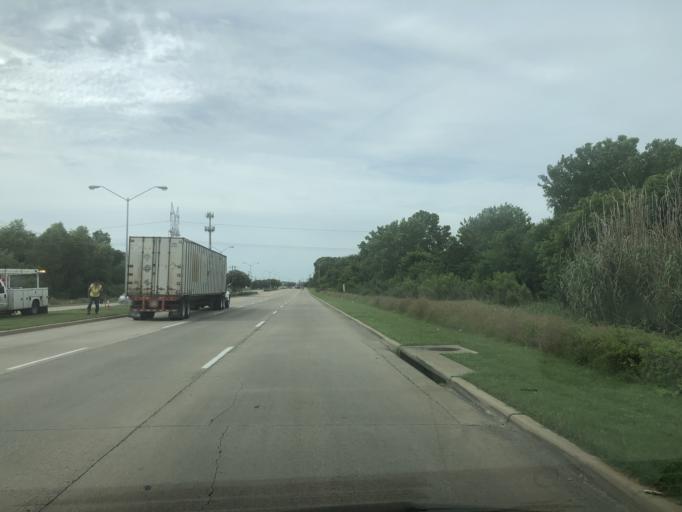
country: US
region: Texas
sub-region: Dallas County
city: Grand Prairie
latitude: 32.7870
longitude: -96.9948
